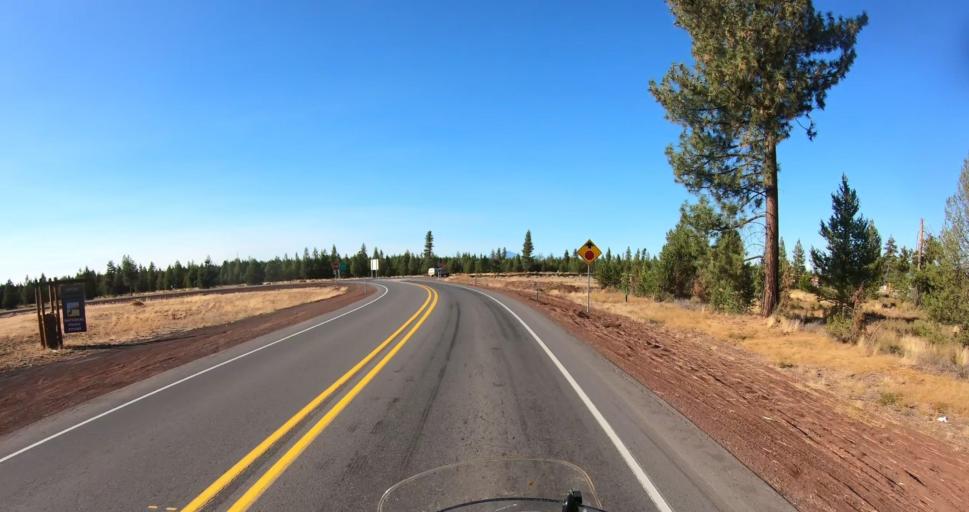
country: US
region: Oregon
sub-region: Deschutes County
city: La Pine
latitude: 43.6466
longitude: -121.5220
